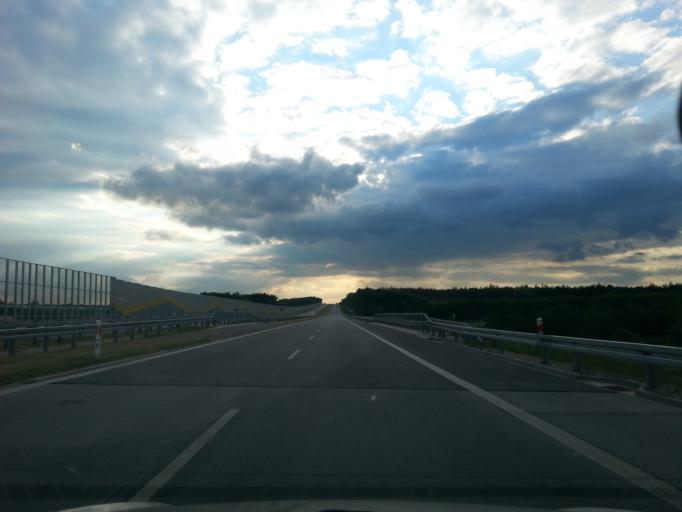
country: PL
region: Lodz Voivodeship
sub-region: Powiat zdunskowolski
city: Zdunska Wola
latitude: 51.5681
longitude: 18.9755
